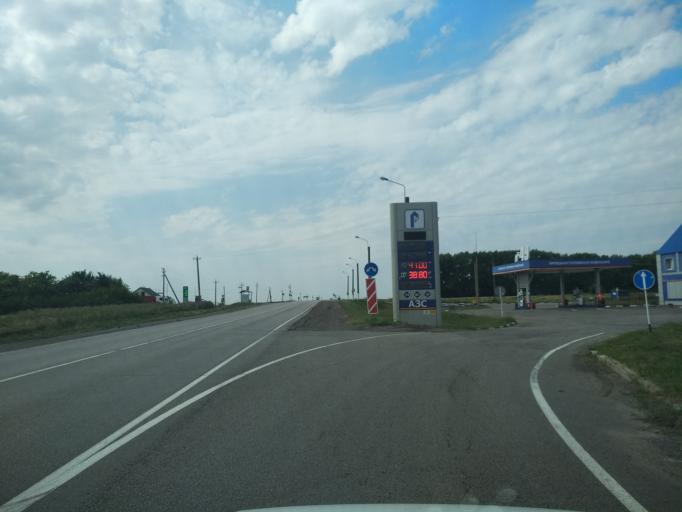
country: RU
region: Lipetsk
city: Dobrinka
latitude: 51.9026
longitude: 40.4555
